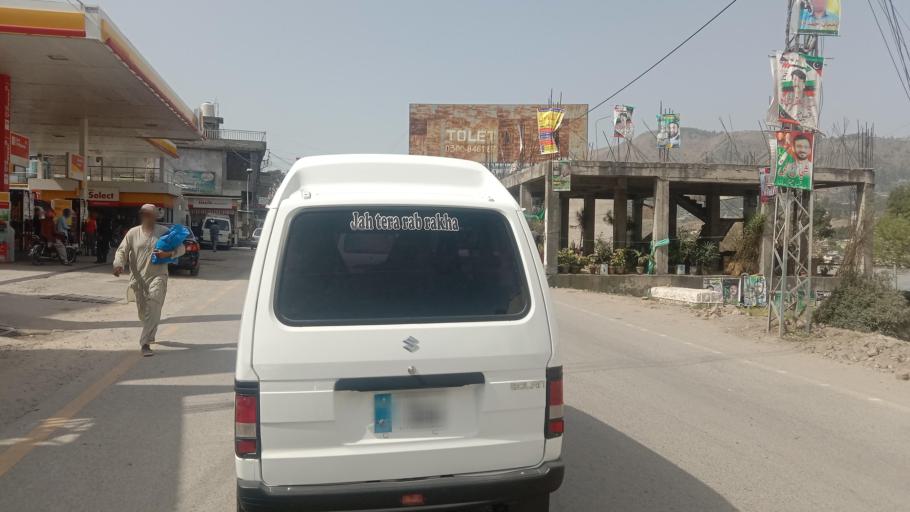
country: PK
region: Khyber Pakhtunkhwa
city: Abbottabad
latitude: 34.1395
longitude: 73.2108
